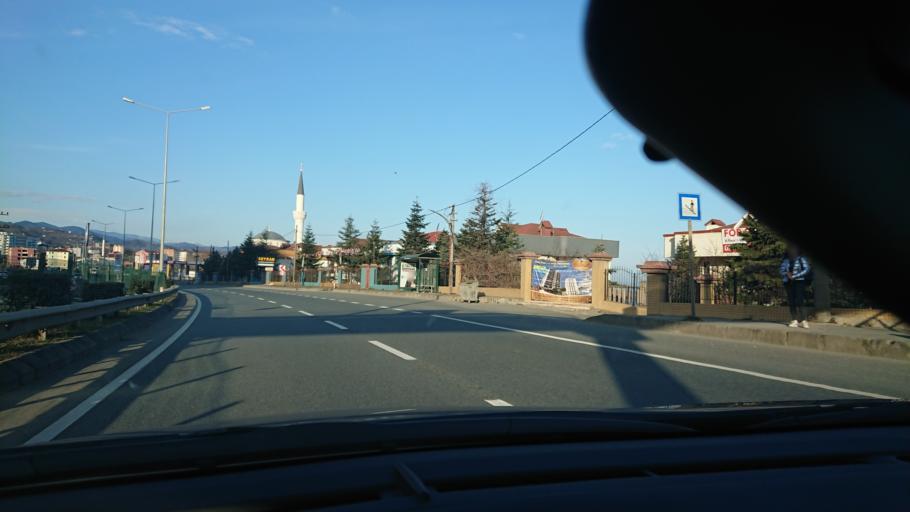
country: TR
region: Trabzon
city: Arsin
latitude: 40.9636
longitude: 39.9916
